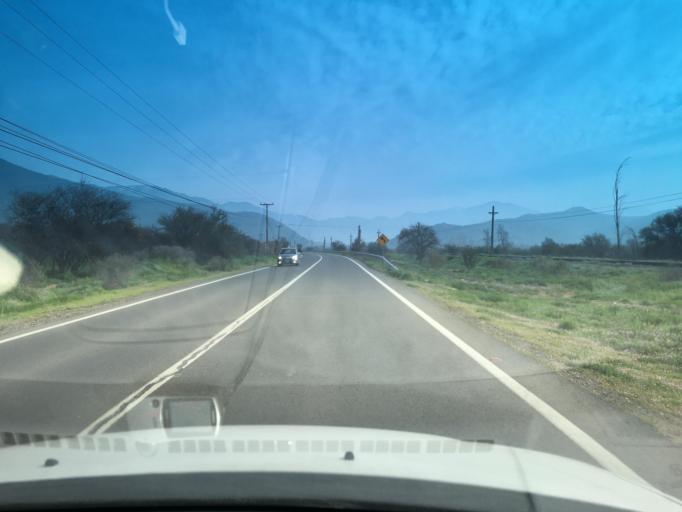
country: CL
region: Santiago Metropolitan
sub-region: Provincia de Chacabuco
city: Lampa
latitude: -33.1553
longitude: -70.9009
